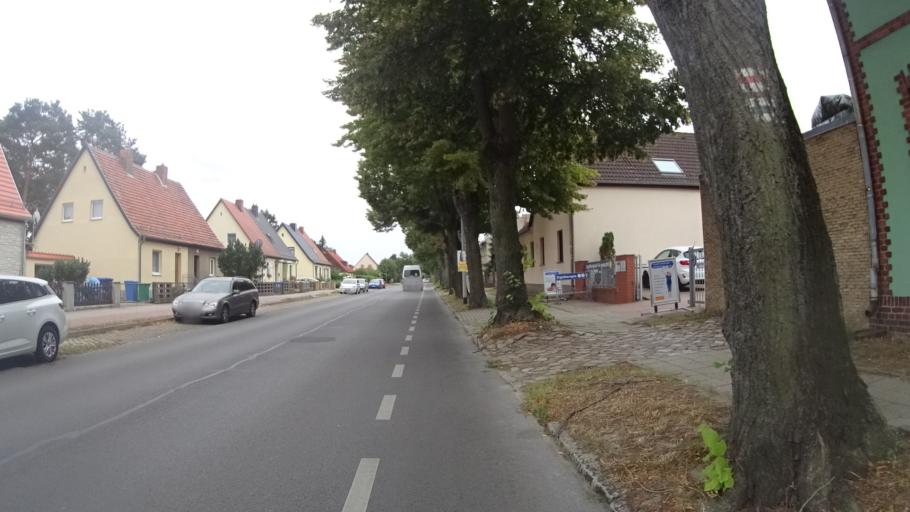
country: DE
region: Brandenburg
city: Luckenwalde
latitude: 52.0993
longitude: 13.1513
